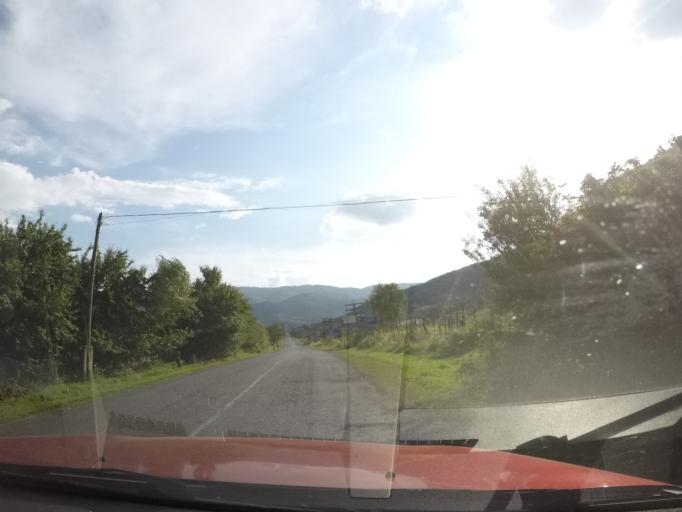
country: UA
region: Zakarpattia
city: Velykyi Bereznyi
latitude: 48.9519
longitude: 22.6092
